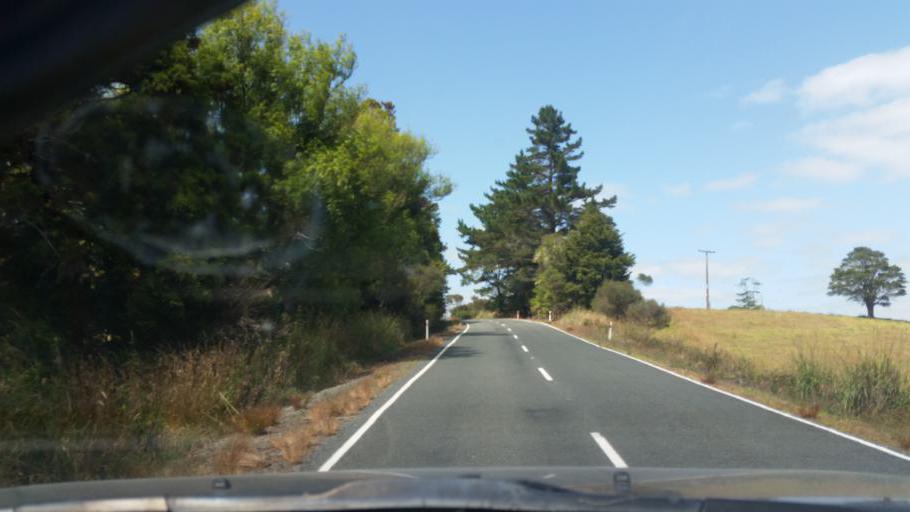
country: NZ
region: Northland
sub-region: Whangarei
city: Ruakaka
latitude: -35.9888
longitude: 174.2931
